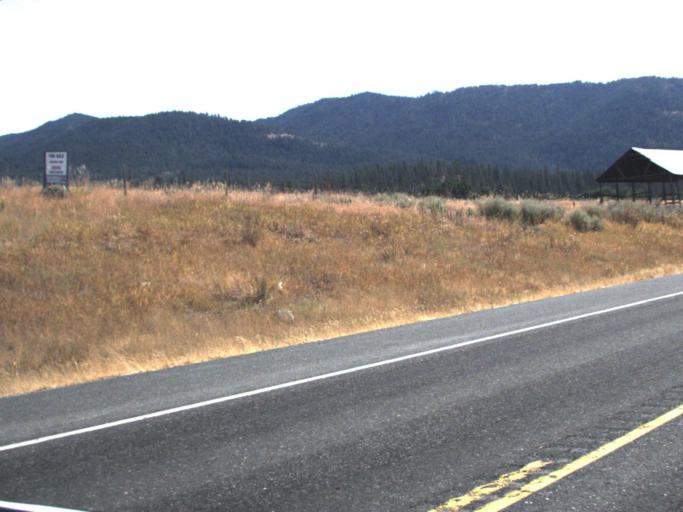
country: US
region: Washington
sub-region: Stevens County
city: Colville
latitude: 48.4182
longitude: -117.8524
